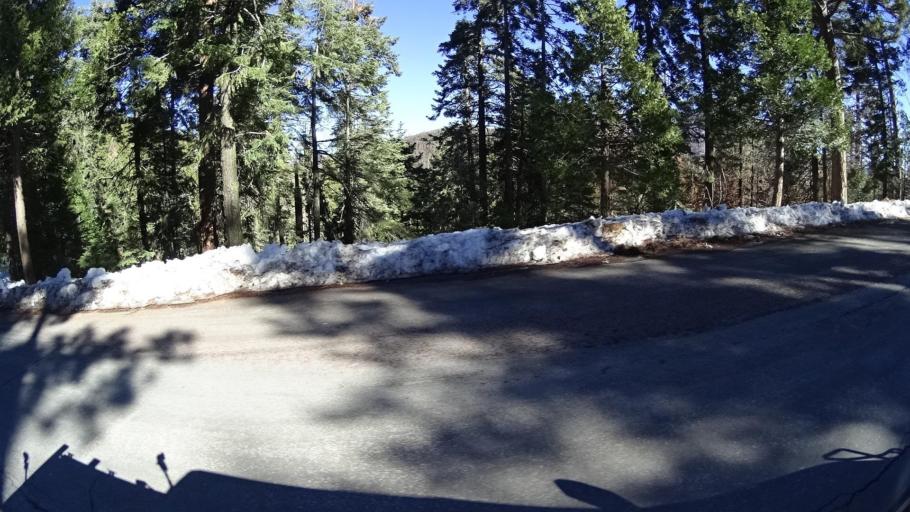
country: US
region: California
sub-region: Kern County
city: Alta Sierra
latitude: 35.7307
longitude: -118.5590
